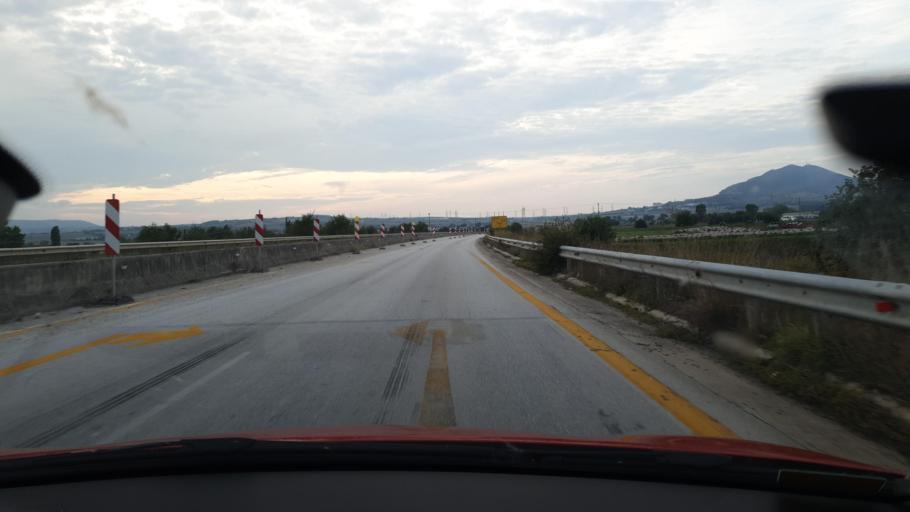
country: GR
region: Central Macedonia
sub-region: Nomos Thessalonikis
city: Assiros
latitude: 40.7841
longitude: 23.0132
